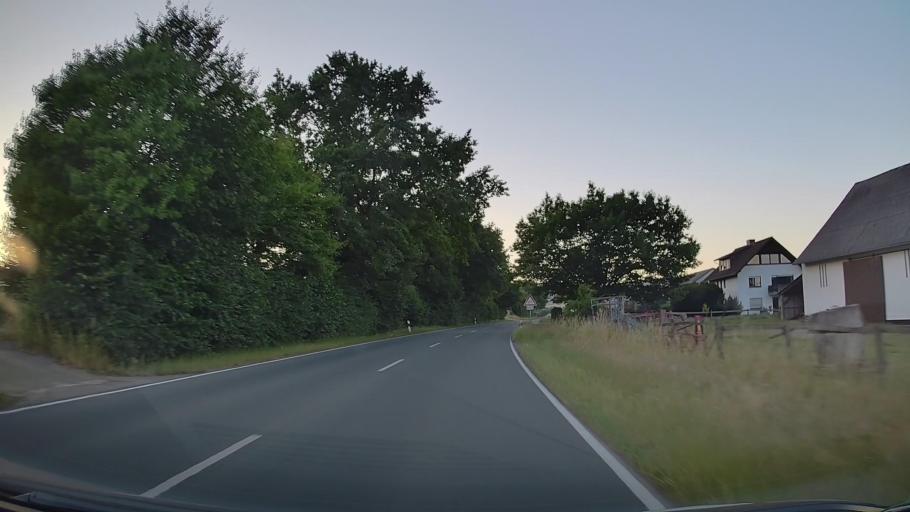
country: DE
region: North Rhine-Westphalia
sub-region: Regierungsbezirk Detmold
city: Lugde
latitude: 51.9670
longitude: 9.2350
